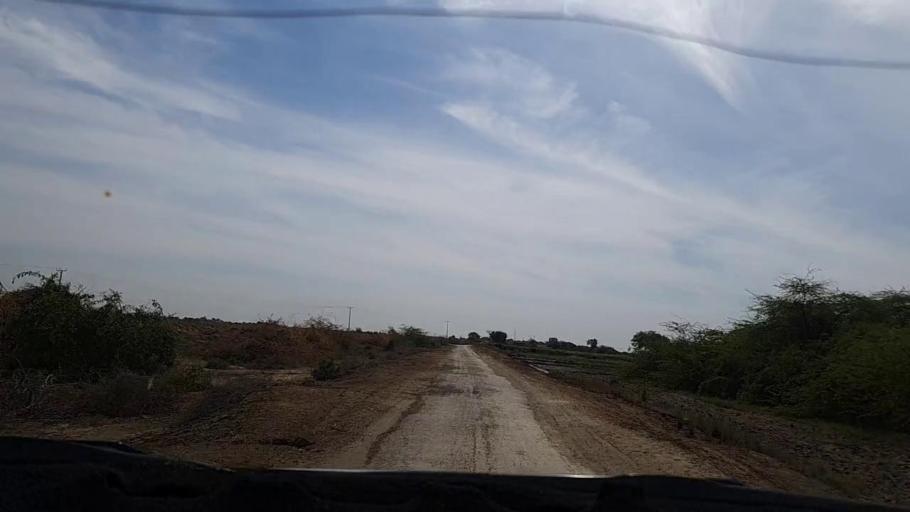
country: PK
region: Sindh
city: Pithoro
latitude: 25.4697
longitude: 69.4566
